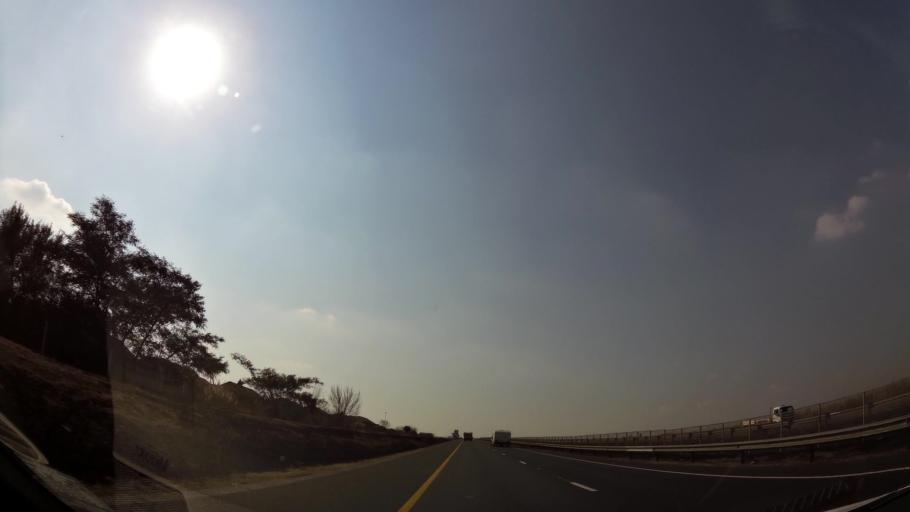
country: ZA
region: Gauteng
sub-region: Ekurhuleni Metropolitan Municipality
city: Brakpan
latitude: -26.1617
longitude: 28.4123
